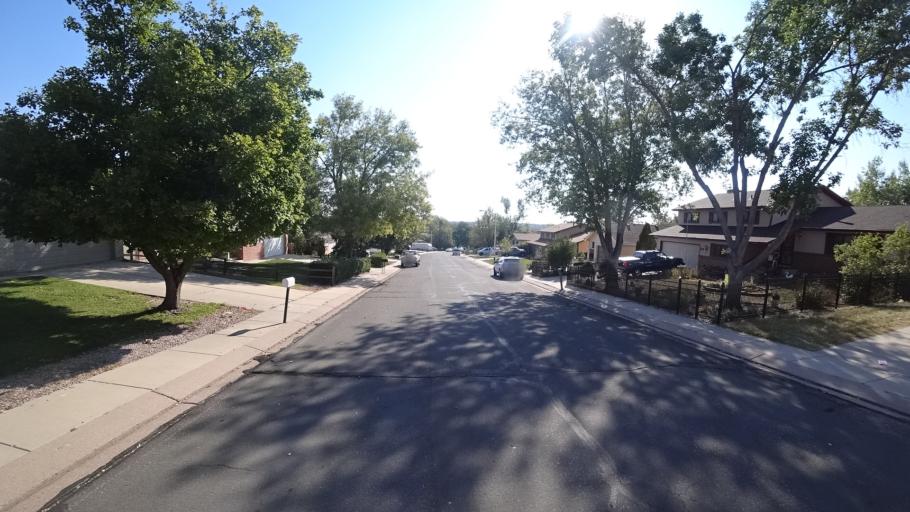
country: US
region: Colorado
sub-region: El Paso County
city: Cimarron Hills
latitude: 38.8811
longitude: -104.7261
